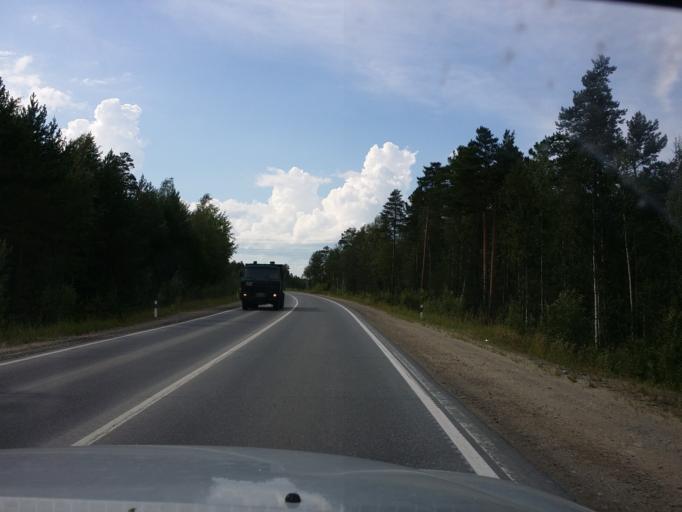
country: RU
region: Khanty-Mansiyskiy Avtonomnyy Okrug
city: Megion
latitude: 61.1245
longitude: 75.8278
